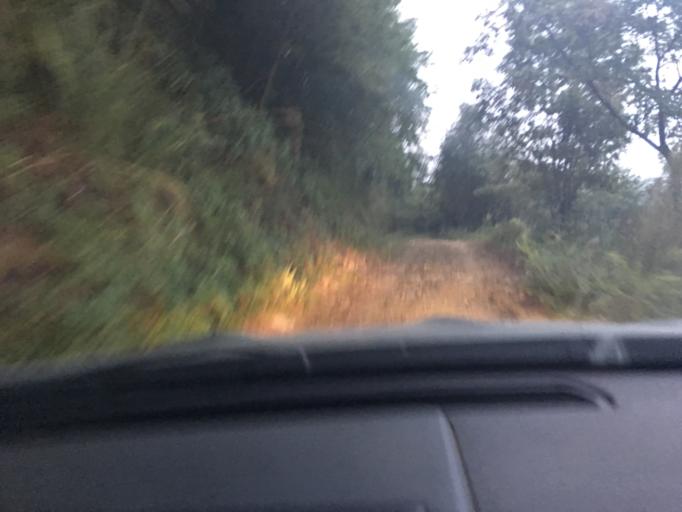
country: CN
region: Guangxi Zhuangzu Zizhiqu
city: Xinzhou
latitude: 24.9044
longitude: 105.5941
